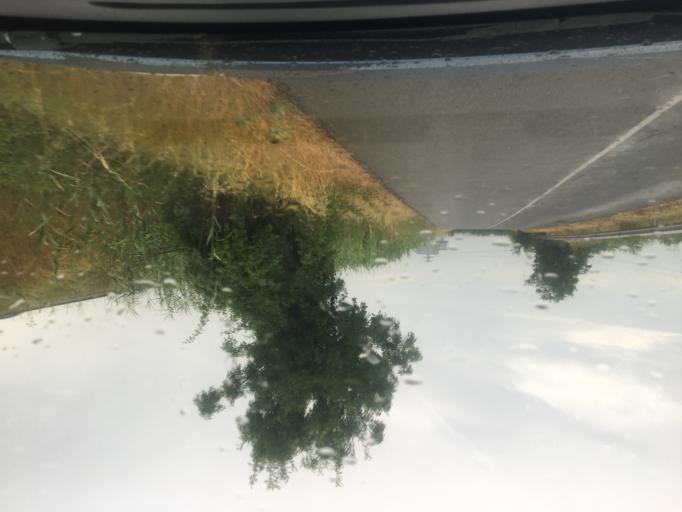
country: BG
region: Burgas
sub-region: Obshtina Burgas
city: Burgas
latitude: 42.5514
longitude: 27.4889
